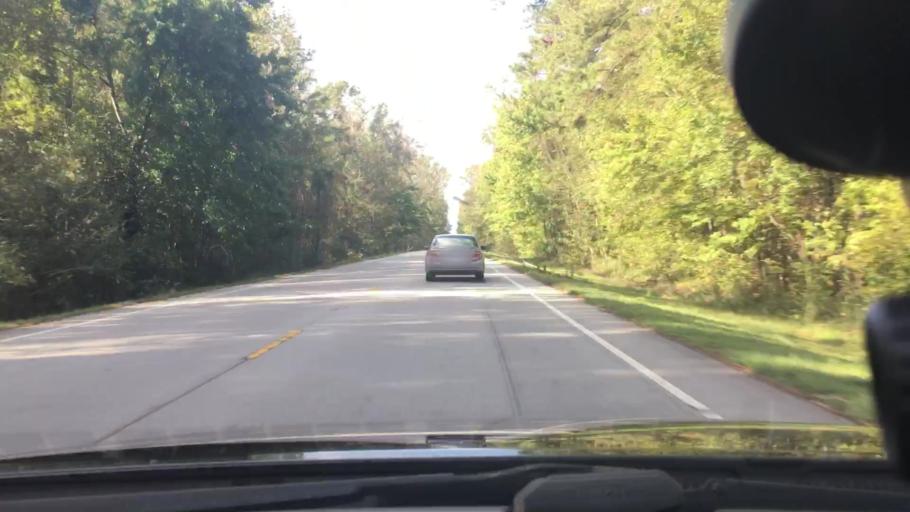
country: US
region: North Carolina
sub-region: Craven County
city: New Bern
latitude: 35.1863
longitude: -77.0502
